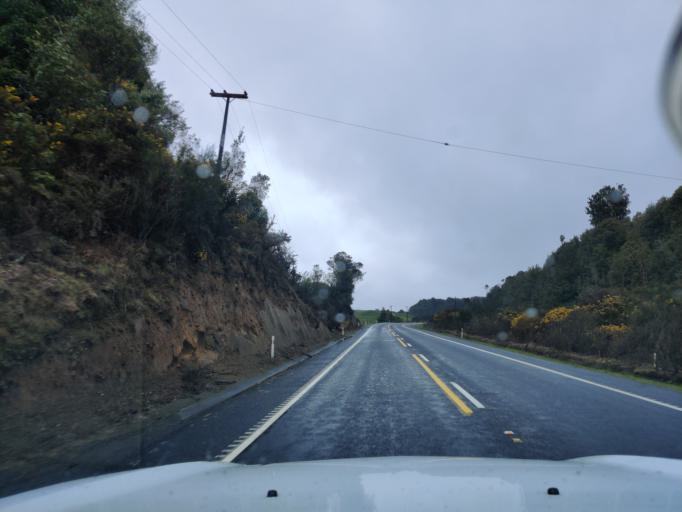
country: NZ
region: Bay of Plenty
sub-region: Rotorua District
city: Rotorua
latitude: -38.0363
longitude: 176.0365
